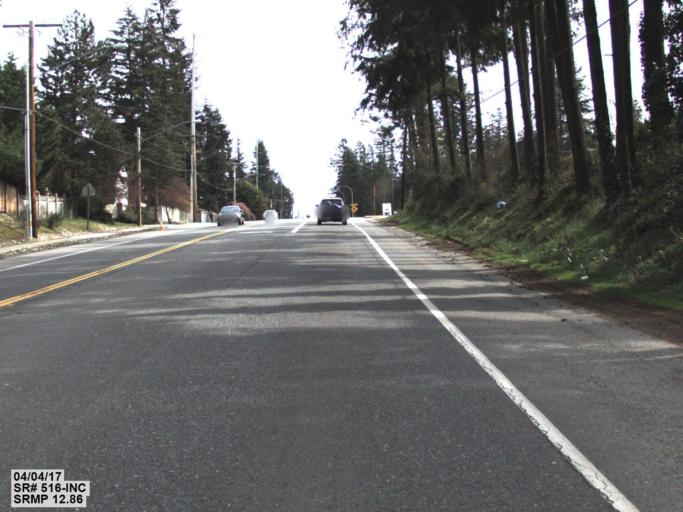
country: US
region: Washington
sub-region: King County
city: Lake Morton-Berrydale
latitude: 47.3581
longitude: -122.0912
